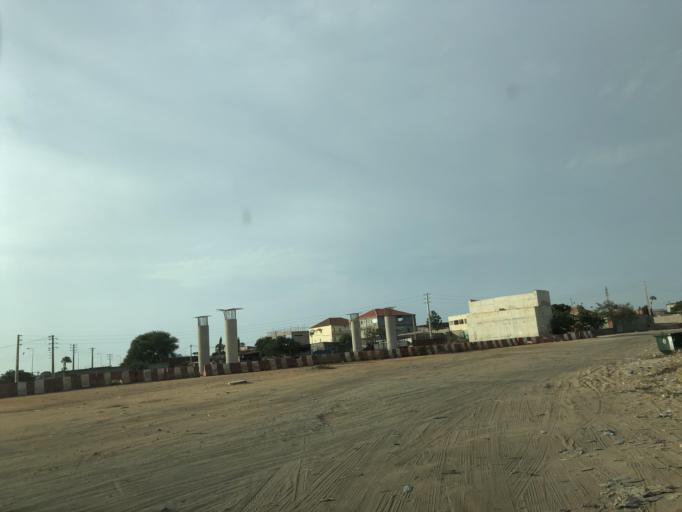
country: AO
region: Luanda
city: Luanda
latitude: -8.9288
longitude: 13.3032
